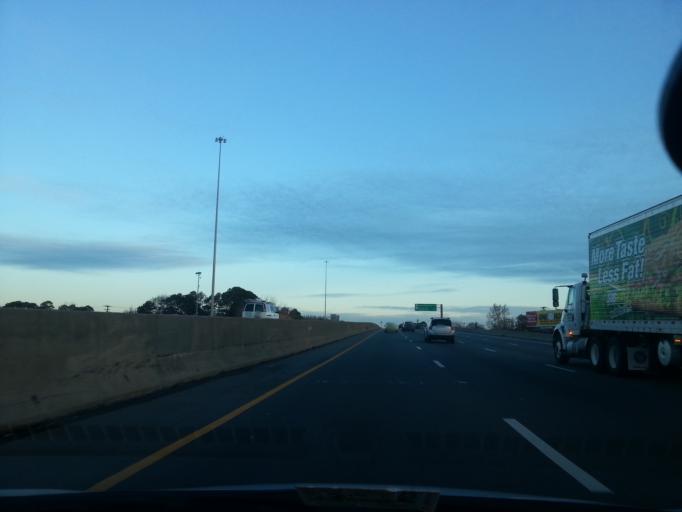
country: US
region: Virginia
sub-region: City of Chesapeake
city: Chesapeake
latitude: 36.8537
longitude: -76.1957
